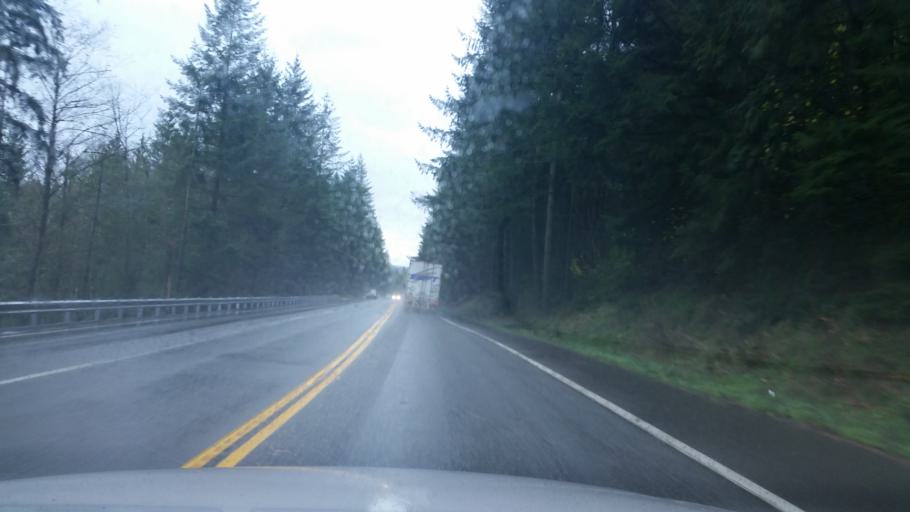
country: US
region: Washington
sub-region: King County
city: Hobart
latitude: 47.4467
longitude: -121.9608
